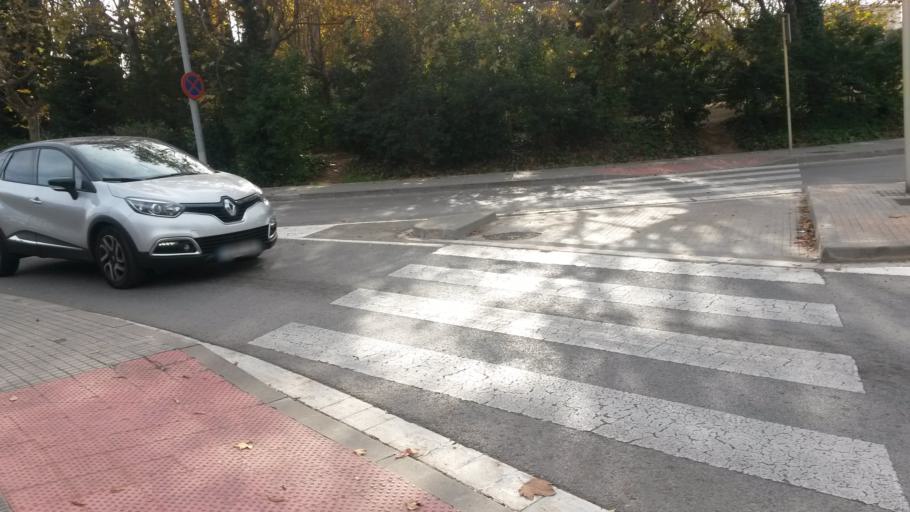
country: ES
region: Catalonia
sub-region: Provincia de Barcelona
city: Cerdanyola del Valles
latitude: 41.4969
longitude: 2.1336
